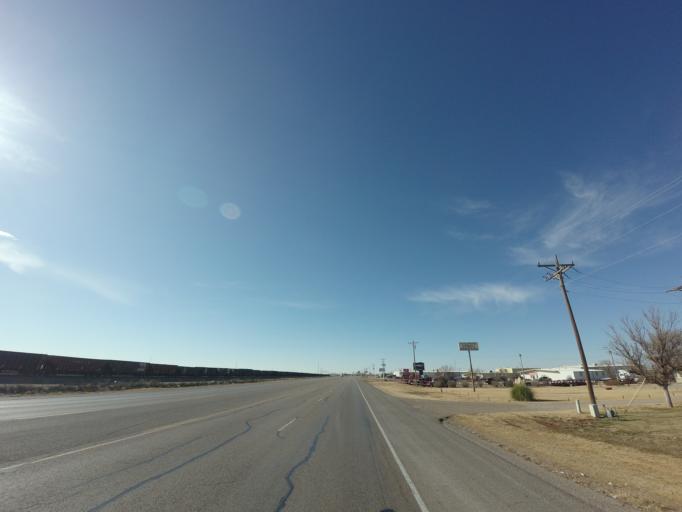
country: US
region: New Mexico
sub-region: Curry County
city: Clovis
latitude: 34.3934
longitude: -103.1325
